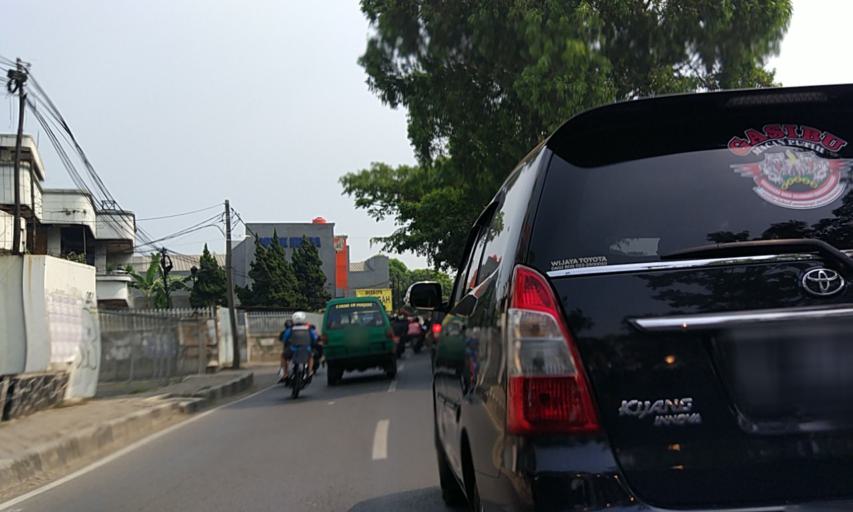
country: ID
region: West Java
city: Bandung
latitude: -6.9162
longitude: 107.5727
